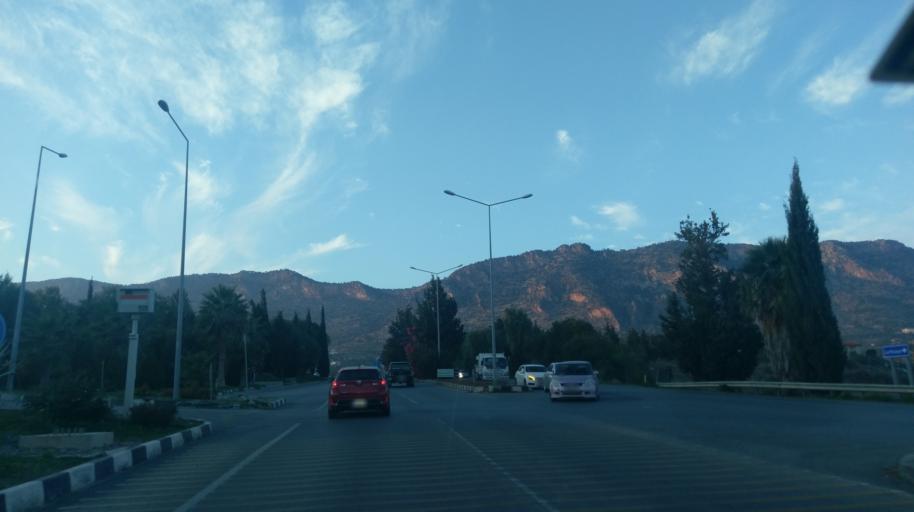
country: CY
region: Keryneia
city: Kyrenia
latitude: 35.2835
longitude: 33.2807
